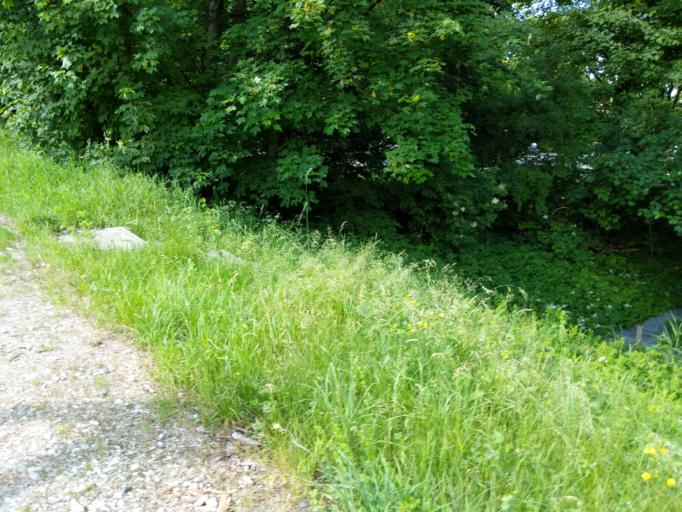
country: DE
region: Bavaria
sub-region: Upper Bavaria
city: Seefeld
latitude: 48.0192
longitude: 11.1973
